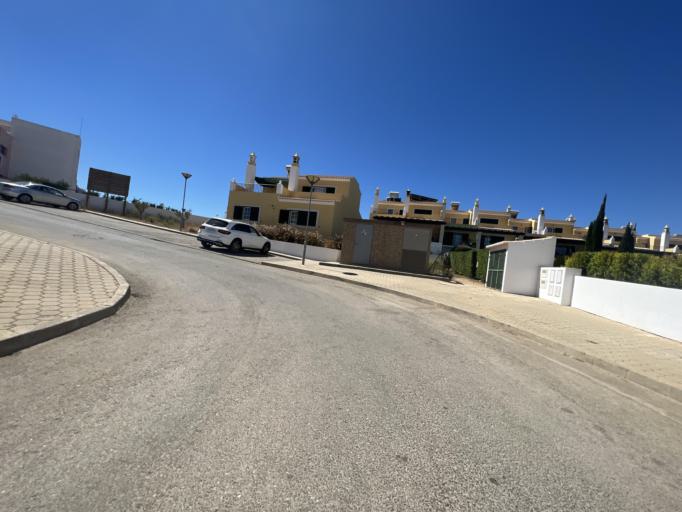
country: PT
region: Faro
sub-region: Portimao
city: Portimao
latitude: 37.1300
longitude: -8.5115
